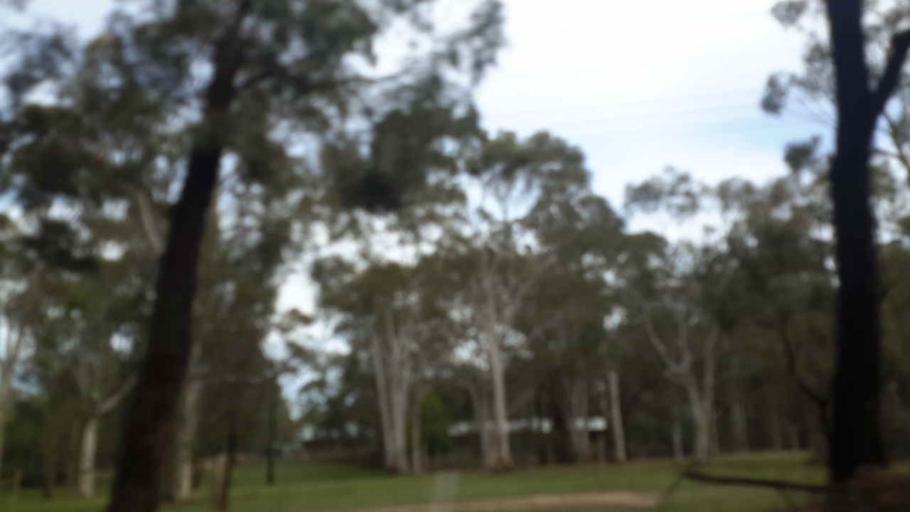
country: AU
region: New South Wales
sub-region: Hawkesbury
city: South Windsor
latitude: -33.6653
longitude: 150.7583
